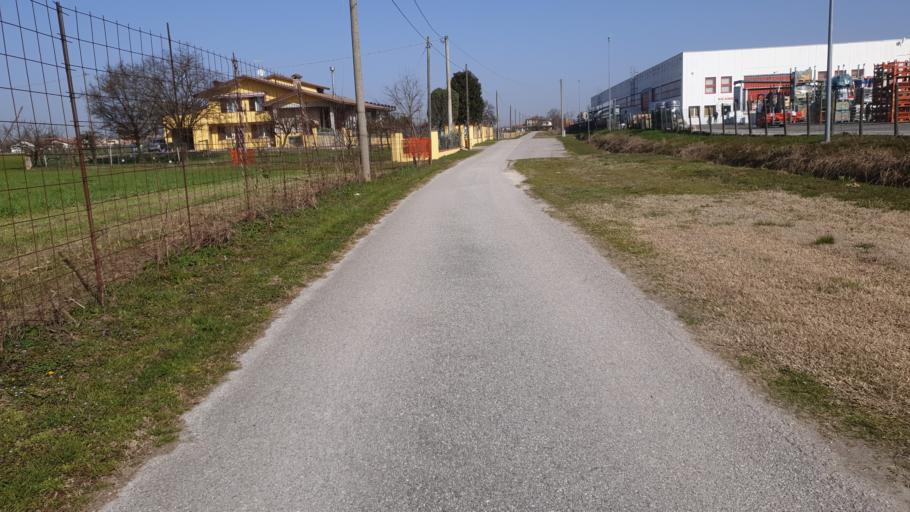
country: IT
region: Veneto
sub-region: Provincia di Padova
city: Cavino
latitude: 45.4975
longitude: 11.8893
